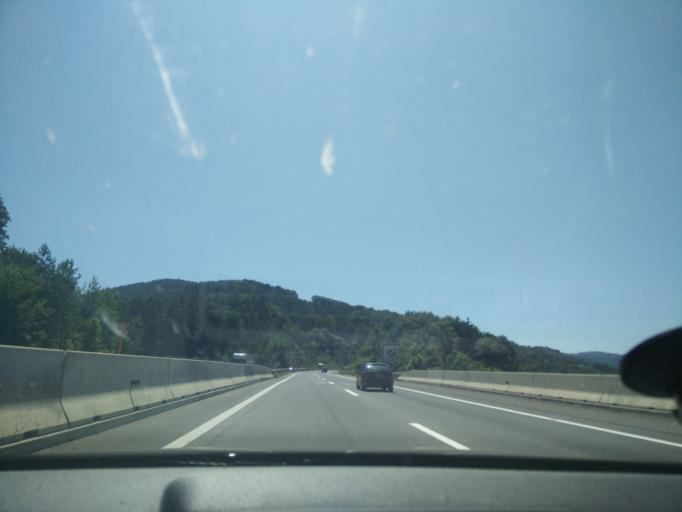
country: AT
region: Lower Austria
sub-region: Politischer Bezirk Neunkirchen
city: Grimmenstein
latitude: 47.6269
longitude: 16.1312
